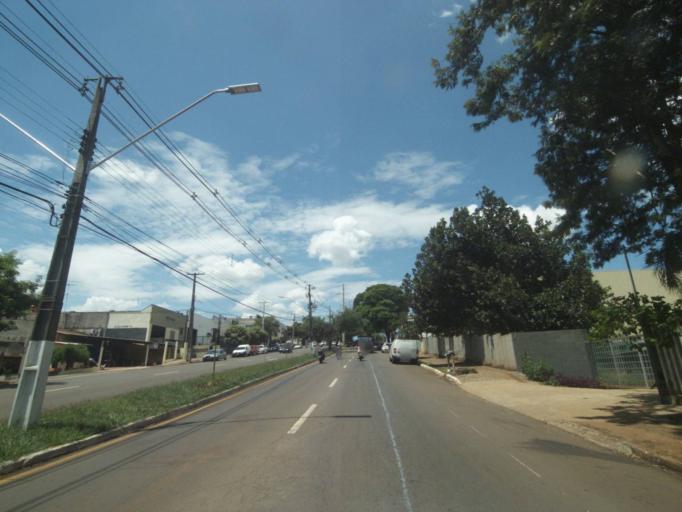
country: BR
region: Parana
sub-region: Londrina
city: Londrina
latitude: -23.3117
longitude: -51.2057
